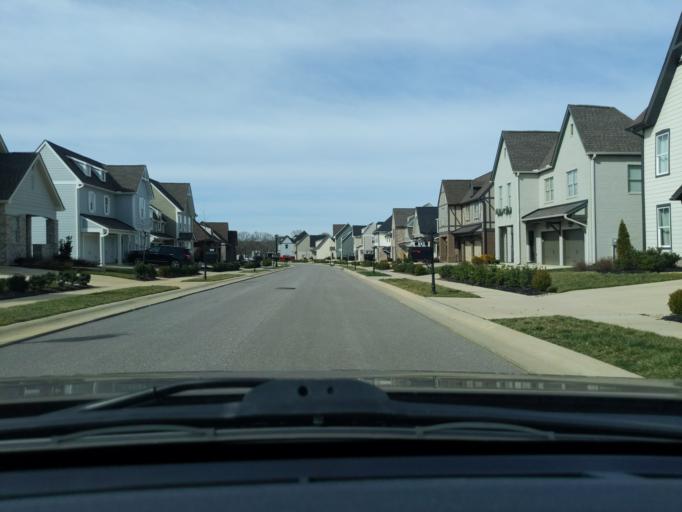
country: US
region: Tennessee
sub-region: Wilson County
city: Mount Juliet
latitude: 36.2141
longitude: -86.4924
